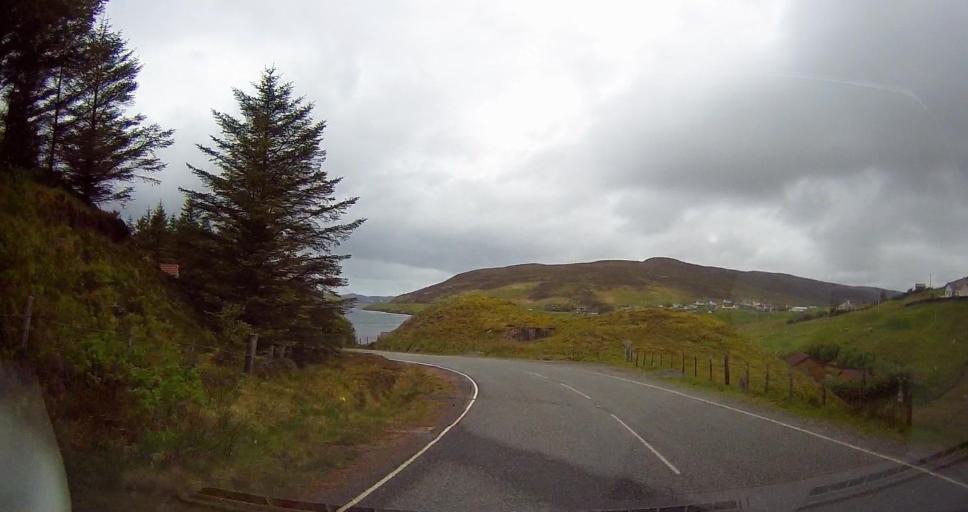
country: GB
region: Scotland
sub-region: Shetland Islands
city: Lerwick
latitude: 60.3499
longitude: -1.2597
